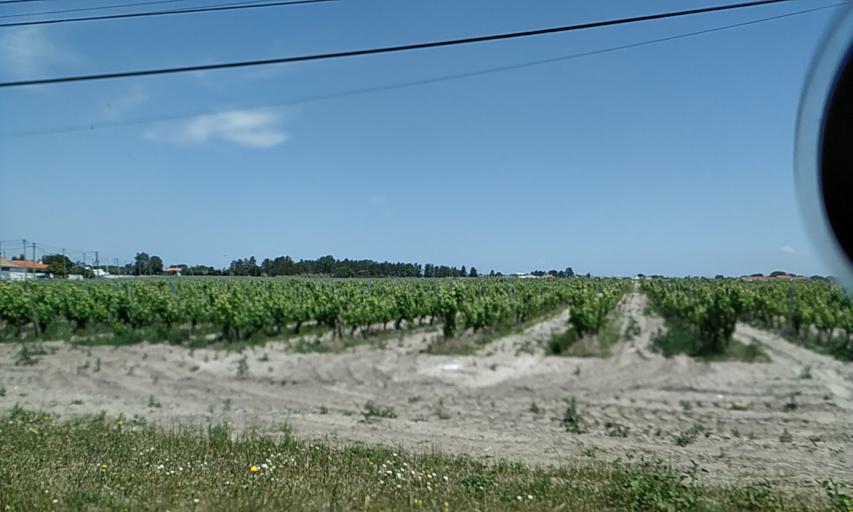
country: PT
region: Setubal
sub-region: Palmela
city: Pinhal Novo
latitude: 38.6382
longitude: -8.7421
